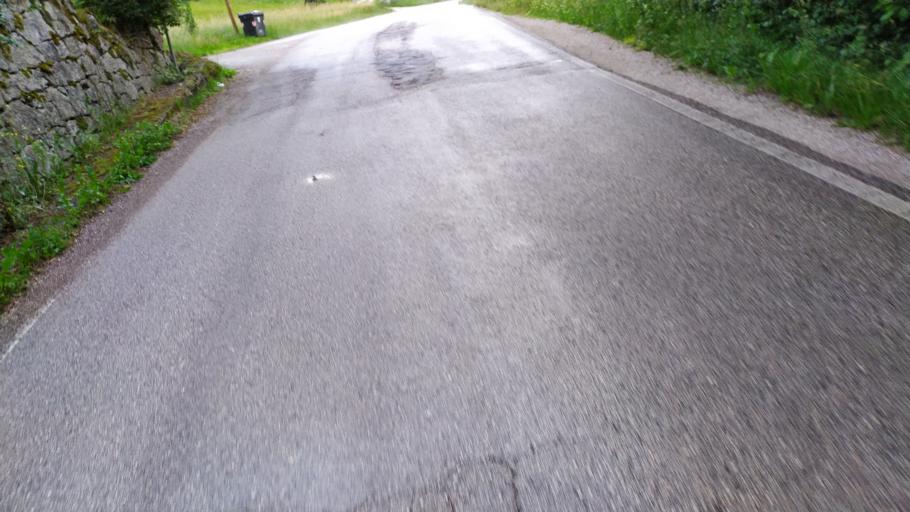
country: IT
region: Veneto
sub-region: Provincia di Vicenza
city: Malo
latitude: 45.6458
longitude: 11.4188
